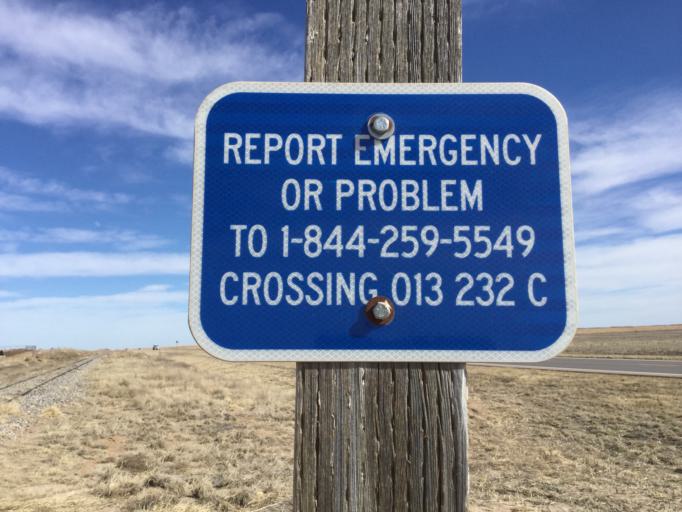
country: US
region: Kansas
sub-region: Stevens County
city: Hugoton
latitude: 37.1305
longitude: -101.5918
